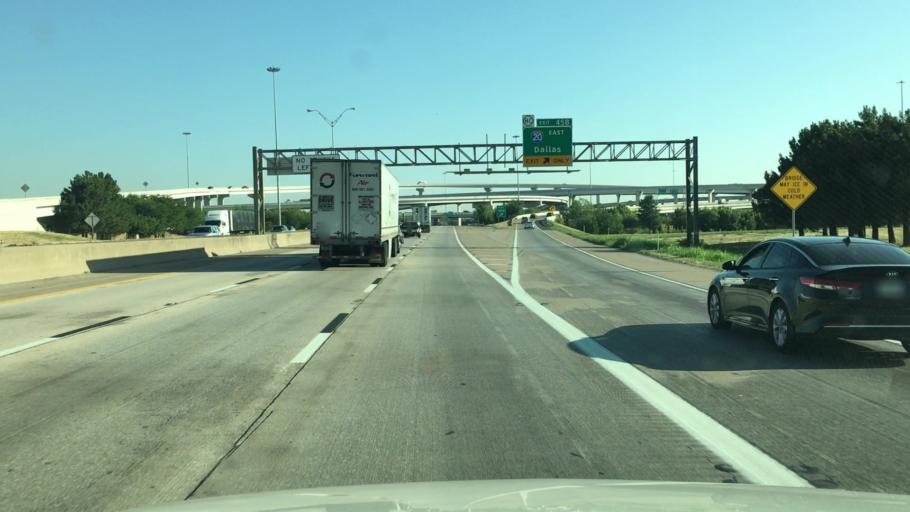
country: US
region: Texas
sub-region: Tarrant County
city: Edgecliff Village
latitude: 32.6624
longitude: -97.3210
